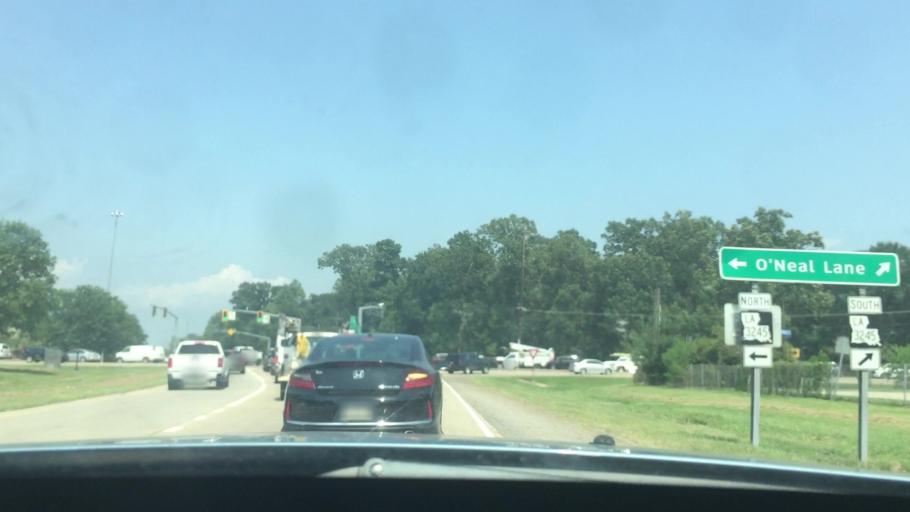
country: US
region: Louisiana
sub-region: East Baton Rouge Parish
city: Shenandoah
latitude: 30.4415
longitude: -91.0085
